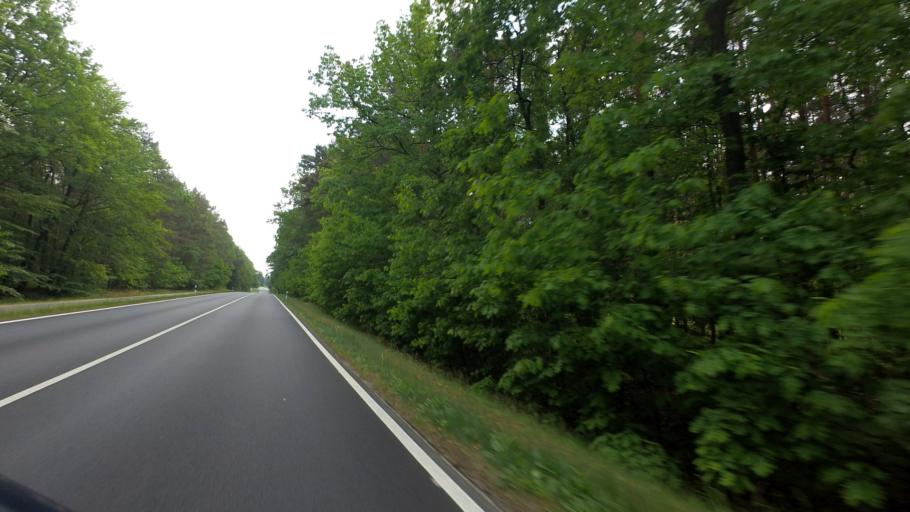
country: DE
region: Saxony
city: Rietschen
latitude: 51.3710
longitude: 14.7941
